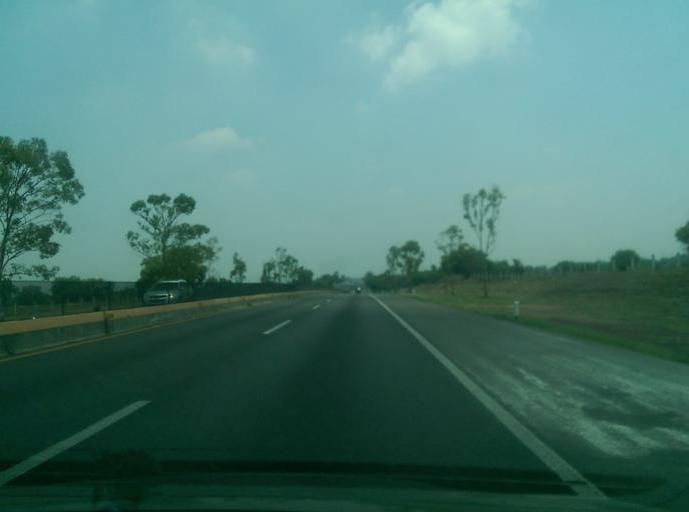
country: MX
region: Morelos
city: Reyes Acozac
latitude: 19.7821
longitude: -98.9472
